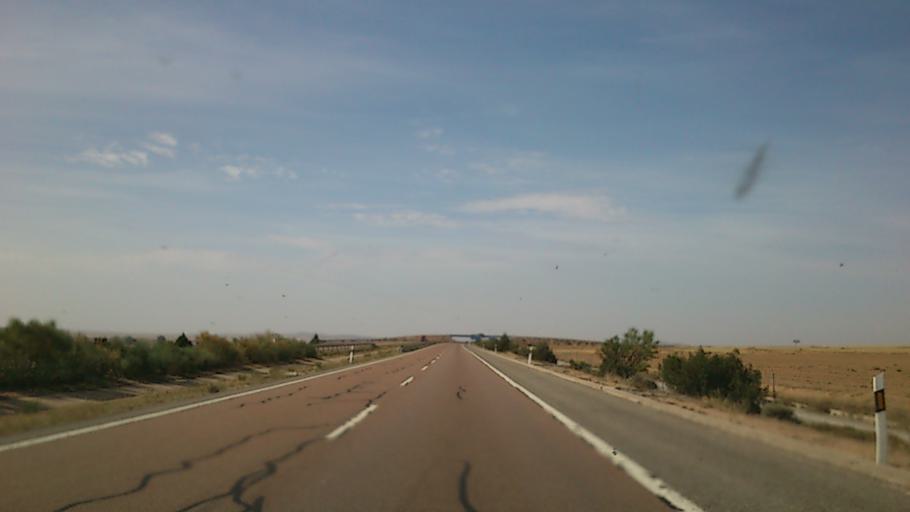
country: ES
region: Aragon
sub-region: Provincia de Teruel
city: Singra
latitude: 40.6837
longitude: -1.3165
